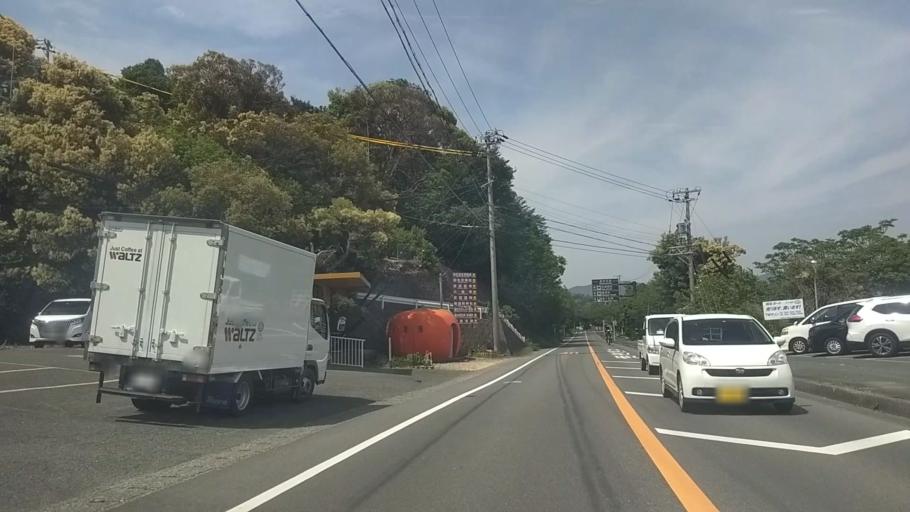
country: JP
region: Shizuoka
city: Kosai-shi
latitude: 34.7759
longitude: 137.5438
